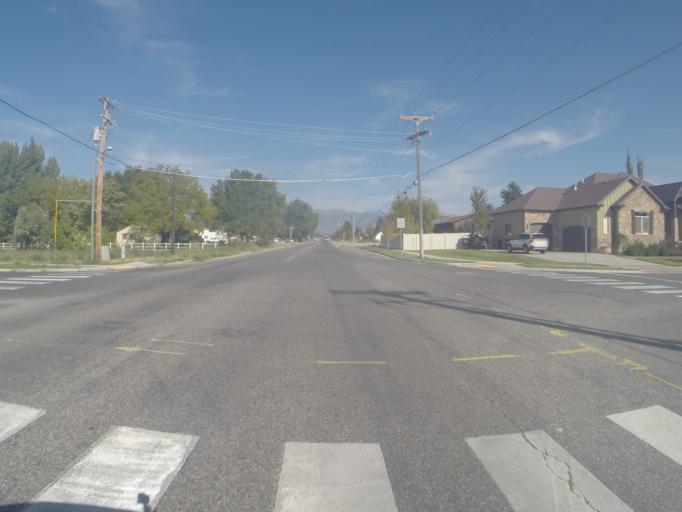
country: US
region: Utah
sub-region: Davis County
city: Syracuse
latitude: 41.0892
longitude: -112.0954
